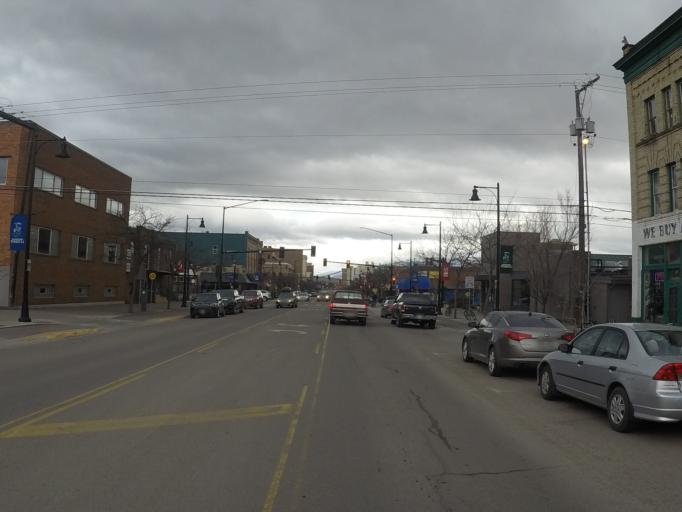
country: US
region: Montana
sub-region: Missoula County
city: Missoula
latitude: 46.8748
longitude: -113.9924
